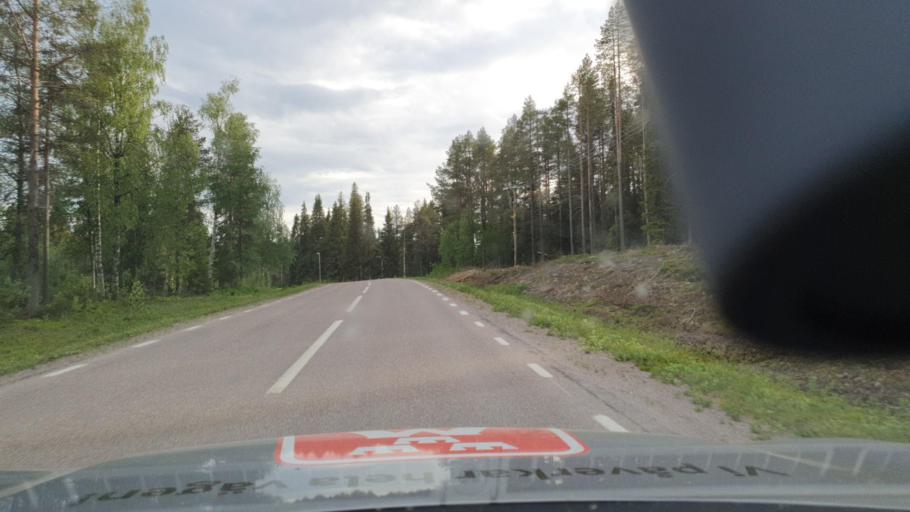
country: SE
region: Norrbotten
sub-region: Gallivare Kommun
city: Gaellivare
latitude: 66.9605
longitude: 21.2390
